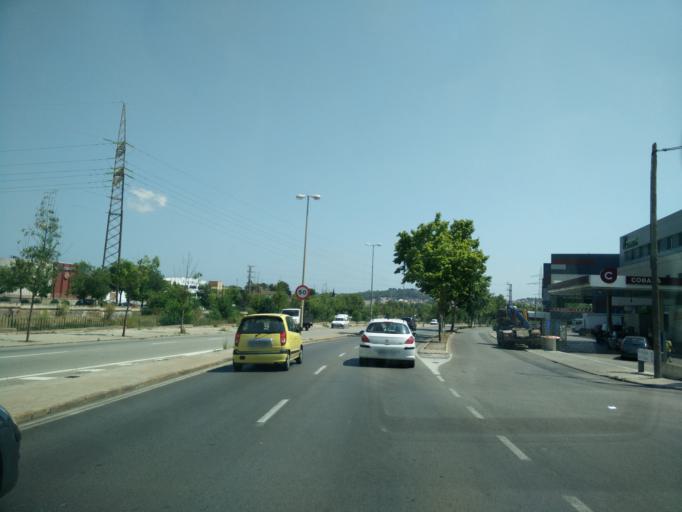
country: ES
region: Catalonia
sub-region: Provincia de Barcelona
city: Terrassa
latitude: 41.5521
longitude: 2.0381
